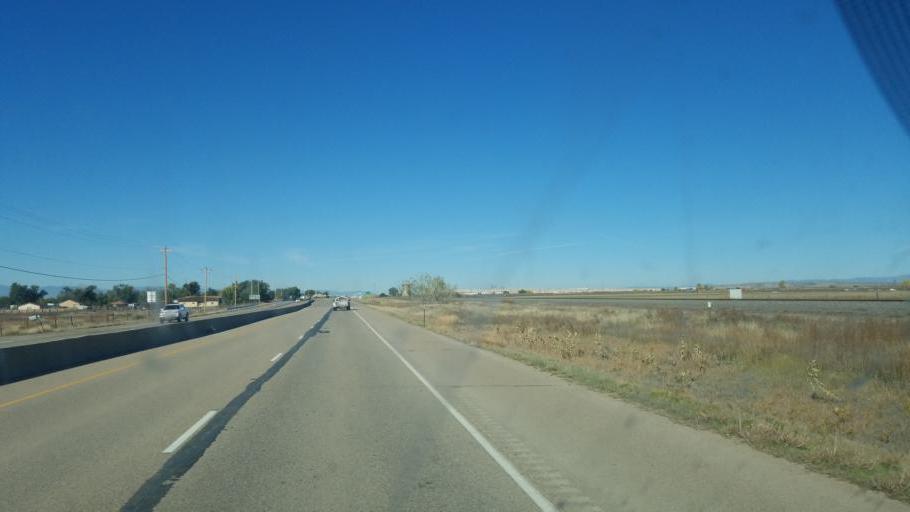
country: US
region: Colorado
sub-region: Pueblo County
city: Pueblo
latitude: 38.2741
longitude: -104.4501
